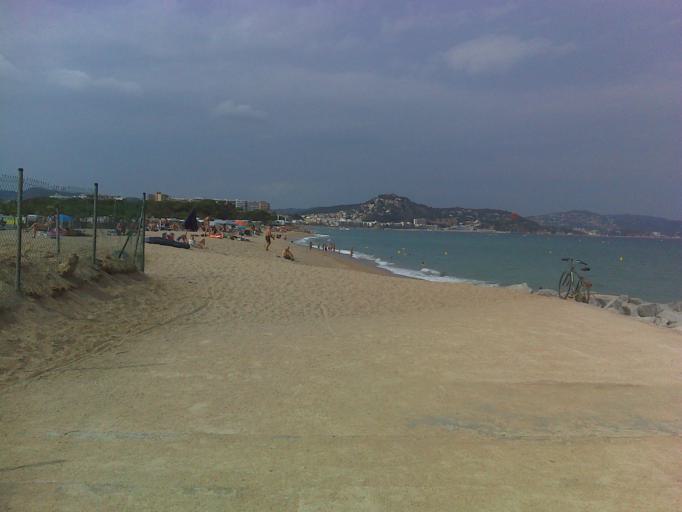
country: ES
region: Catalonia
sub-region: Provincia de Girona
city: Blanes
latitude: 41.6517
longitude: 2.7785
